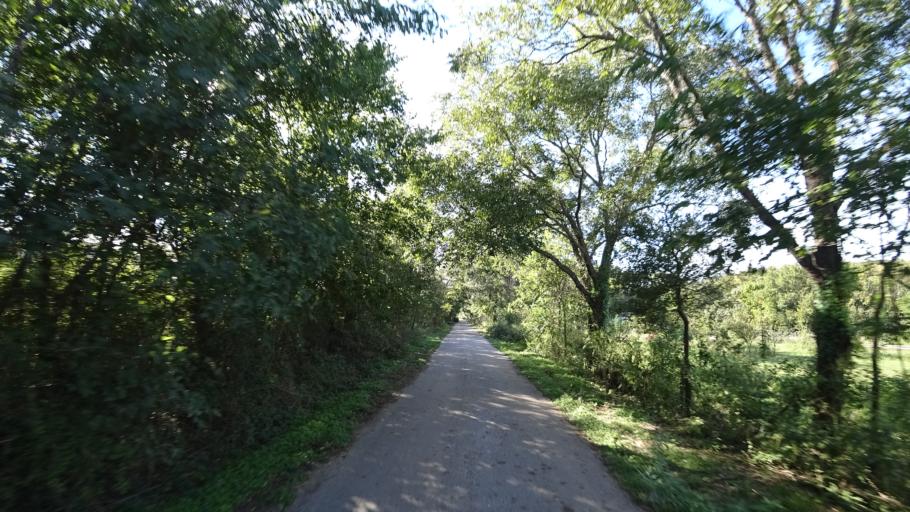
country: US
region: Texas
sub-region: Travis County
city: Austin
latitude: 30.2617
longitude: -97.6668
